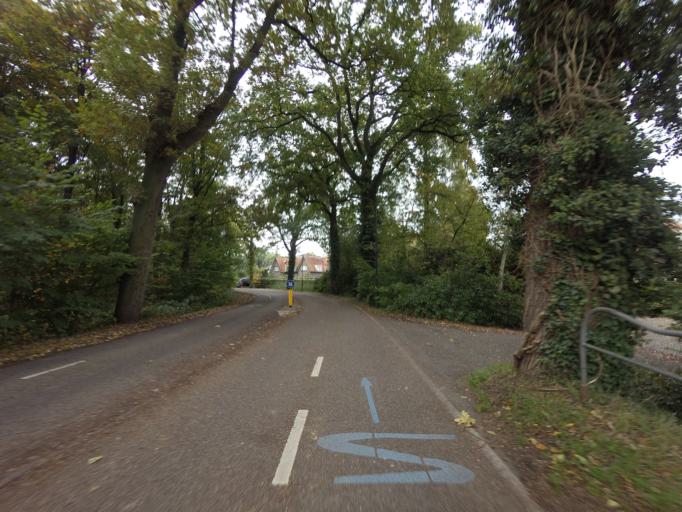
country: NL
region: North Brabant
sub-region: Gemeente Breda
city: Breda
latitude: 51.5648
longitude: 4.7548
